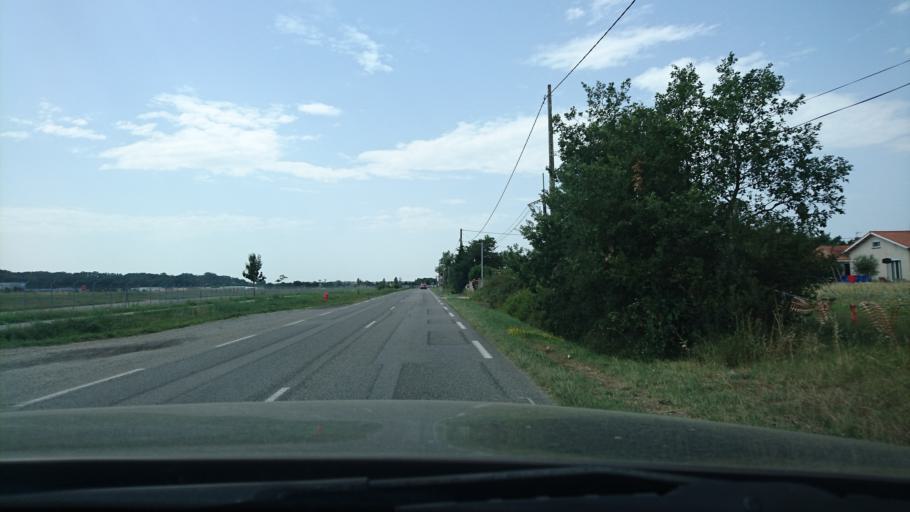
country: FR
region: Midi-Pyrenees
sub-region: Departement de la Haute-Garonne
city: Cornebarrieu
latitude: 43.6475
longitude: 1.3466
